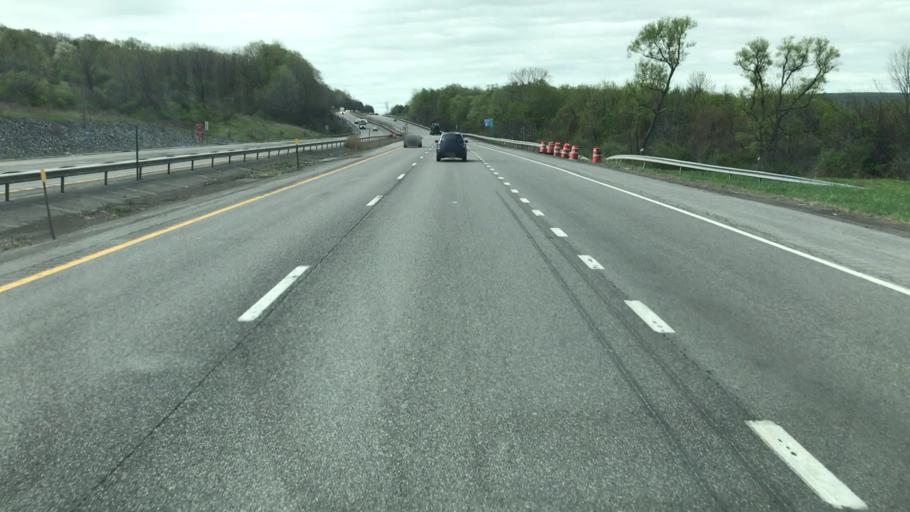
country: US
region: New York
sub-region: Onondaga County
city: Nedrow
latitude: 42.8547
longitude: -76.1196
